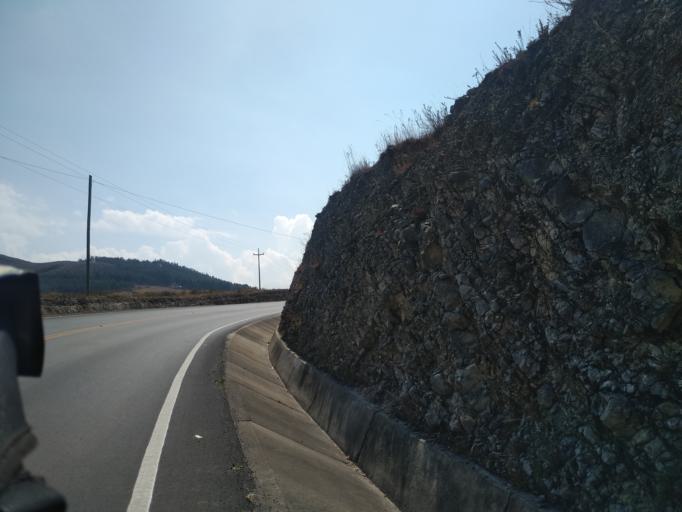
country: PE
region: Cajamarca
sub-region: Provincia de Cajamarca
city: Llacanora
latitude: -7.2061
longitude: -78.3846
